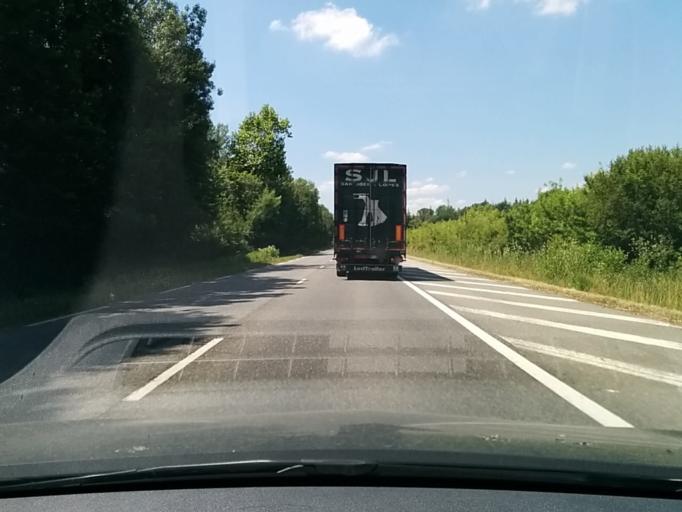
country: FR
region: Midi-Pyrenees
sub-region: Departement du Gers
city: Auch
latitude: 43.6785
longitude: 0.5081
